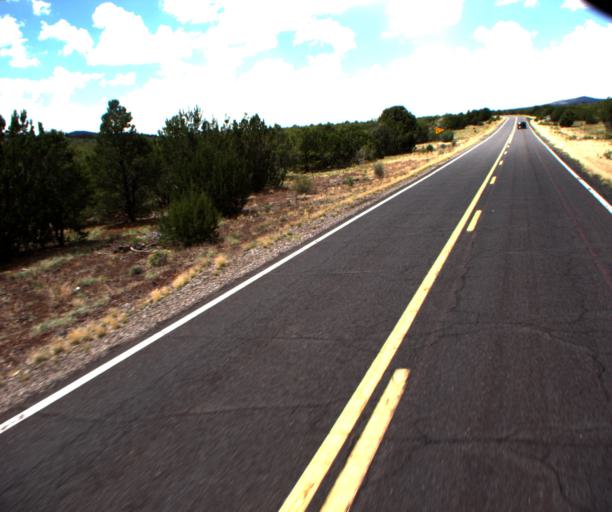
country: US
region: Arizona
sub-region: Coconino County
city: Parks
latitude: 35.5617
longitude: -111.8821
